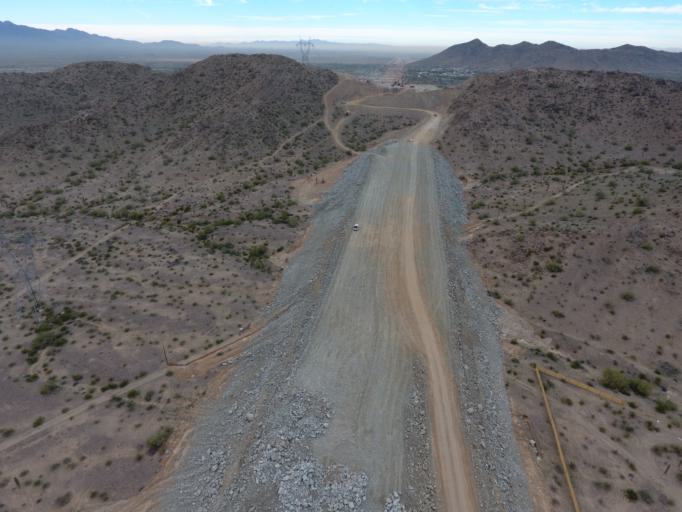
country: US
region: Arizona
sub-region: Maricopa County
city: Laveen
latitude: 33.3010
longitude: -112.1418
